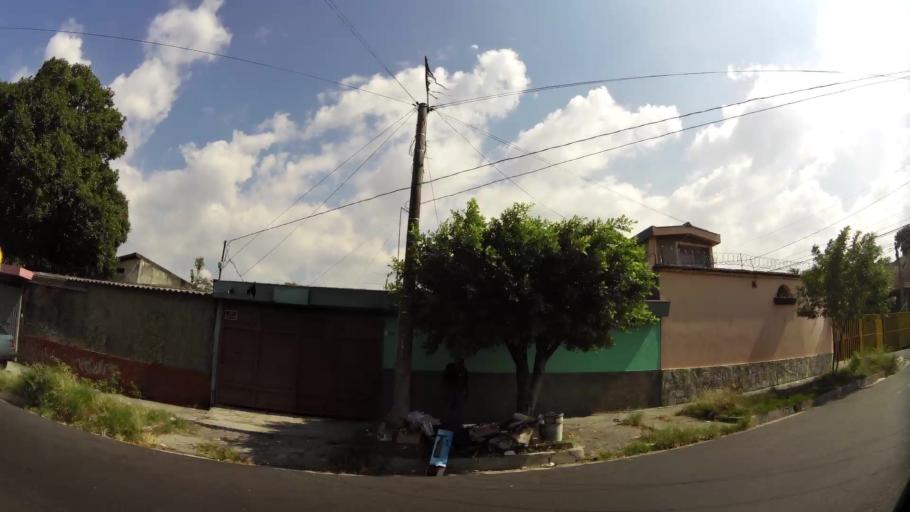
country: SV
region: San Salvador
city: Mejicanos
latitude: 13.7220
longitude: -89.2120
